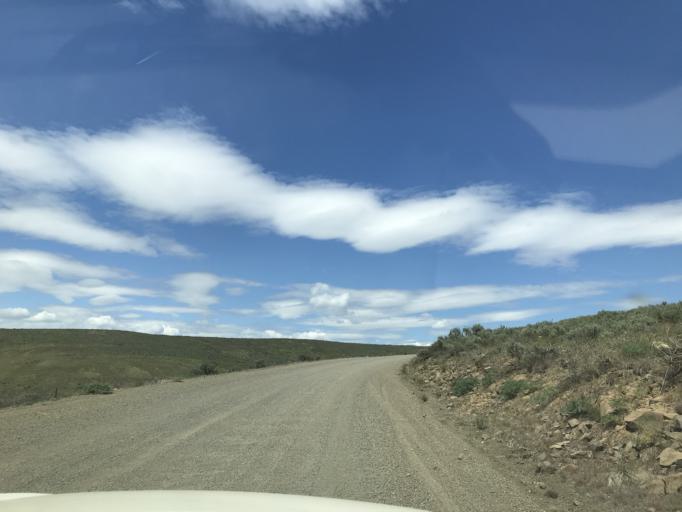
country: US
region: Washington
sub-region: Grant County
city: Quincy
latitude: 47.3086
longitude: -119.8257
